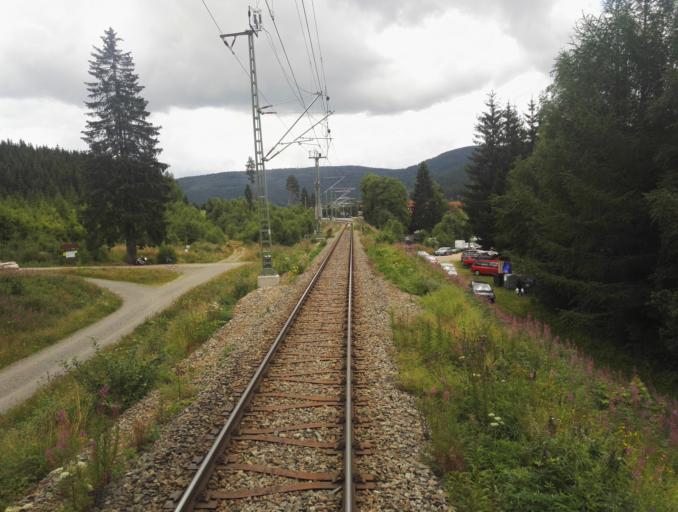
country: DE
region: Baden-Wuerttemberg
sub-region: Freiburg Region
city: Schluchsee
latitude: 47.8366
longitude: 8.1326
